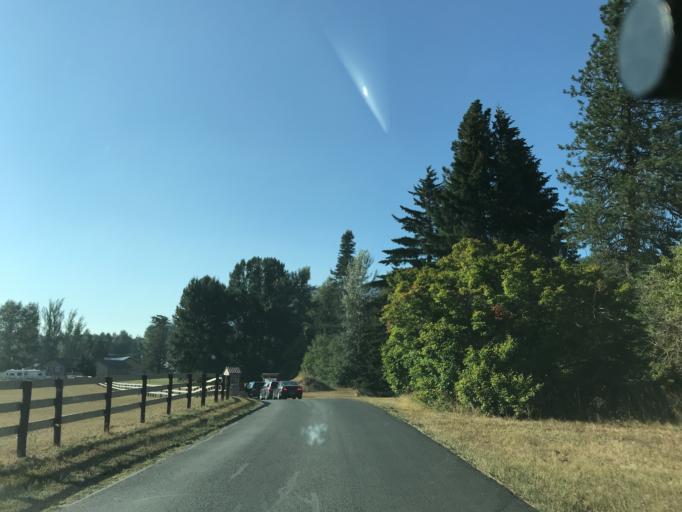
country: US
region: Washington
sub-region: Kittitas County
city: Cle Elum
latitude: 47.2107
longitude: -121.0945
